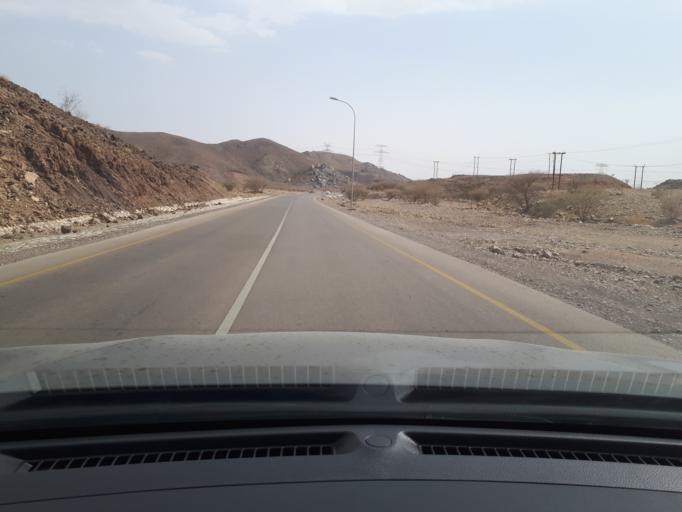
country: OM
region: Ash Sharqiyah
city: Badiyah
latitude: 22.5316
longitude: 58.9559
